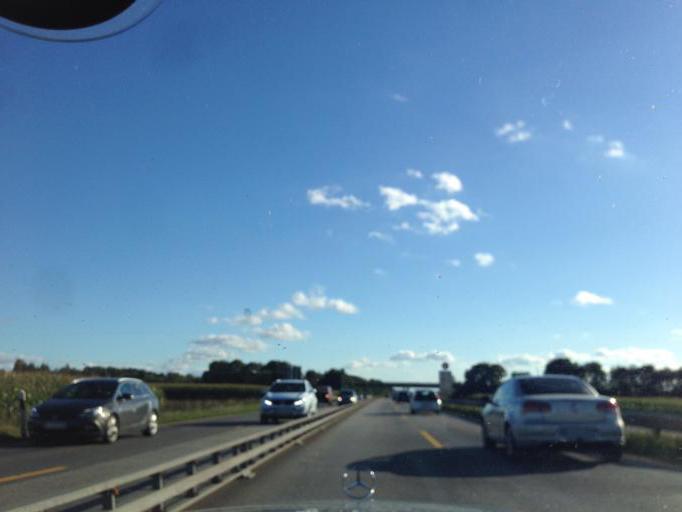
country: DE
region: Schleswig-Holstein
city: Loop
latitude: 54.1498
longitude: 9.9643
